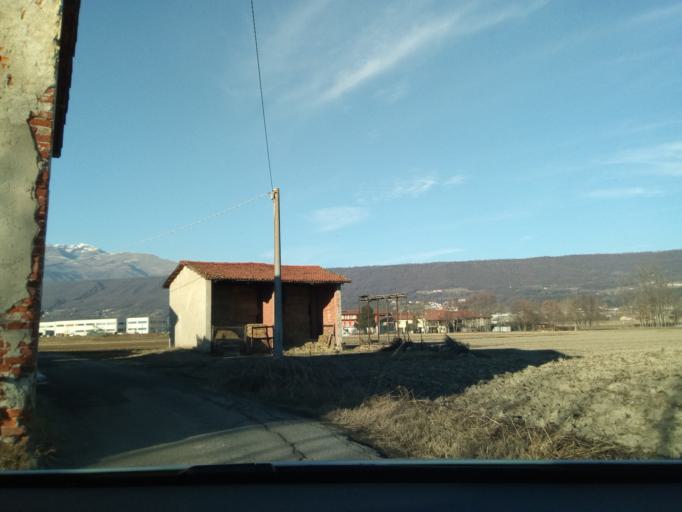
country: IT
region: Piedmont
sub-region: Provincia di Torino
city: Burolo
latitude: 45.4639
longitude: 7.9210
